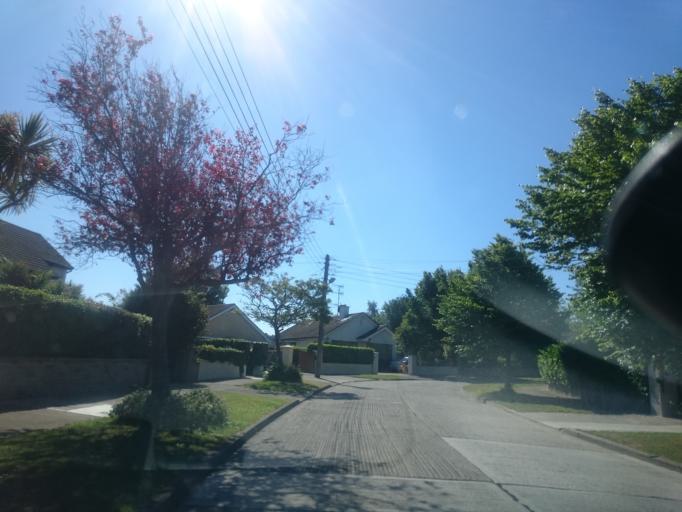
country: IE
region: Leinster
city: Sallynoggin
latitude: 53.2721
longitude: -6.1304
